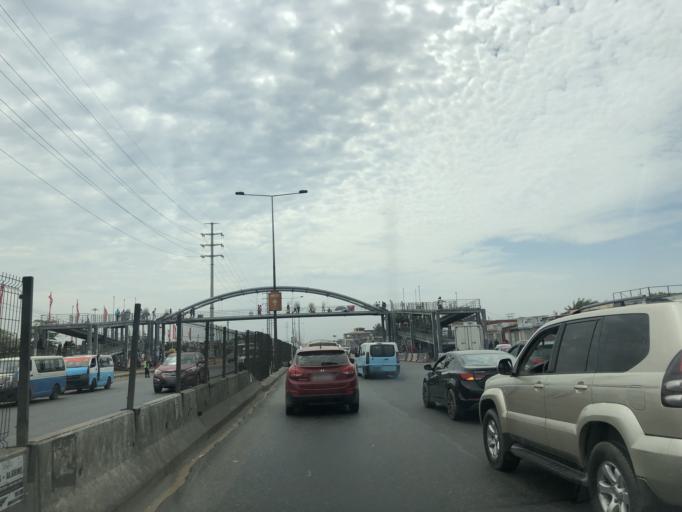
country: AO
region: Luanda
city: Luanda
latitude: -8.8479
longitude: 13.2828
